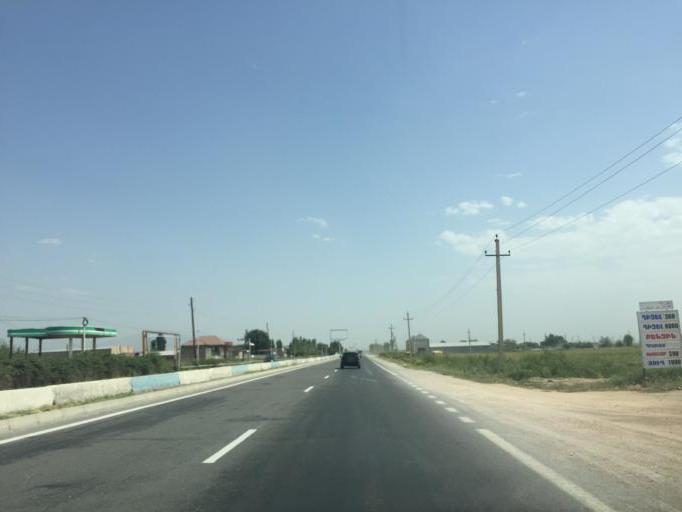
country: AM
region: Ararat
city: Artashat
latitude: 39.9461
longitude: 44.5486
